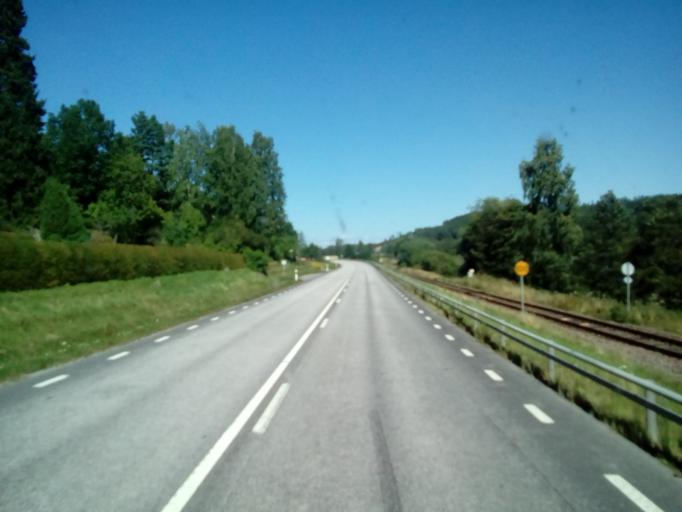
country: SE
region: OEstergoetland
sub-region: Kinda Kommun
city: Kisa
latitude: 58.0130
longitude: 15.6460
